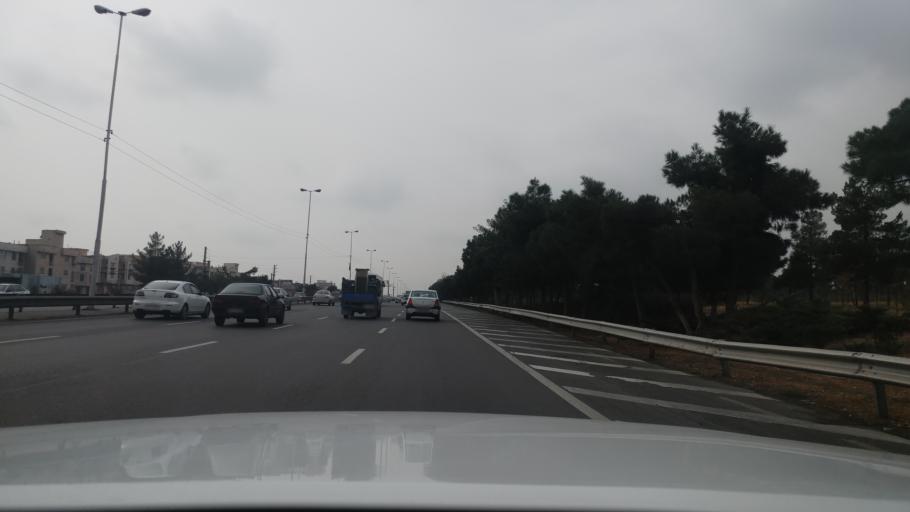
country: IR
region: Tehran
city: Tehran
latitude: 35.7158
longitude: 51.2790
